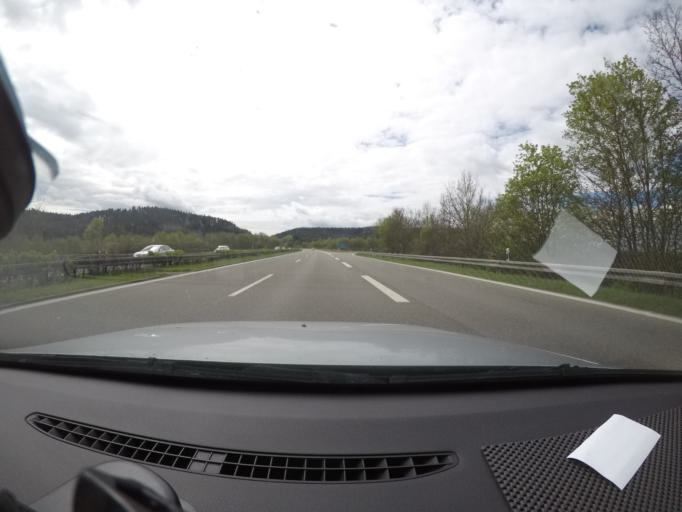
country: DE
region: Baden-Wuerttemberg
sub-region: Freiburg Region
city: Vohringen
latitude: 48.2987
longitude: 8.6347
